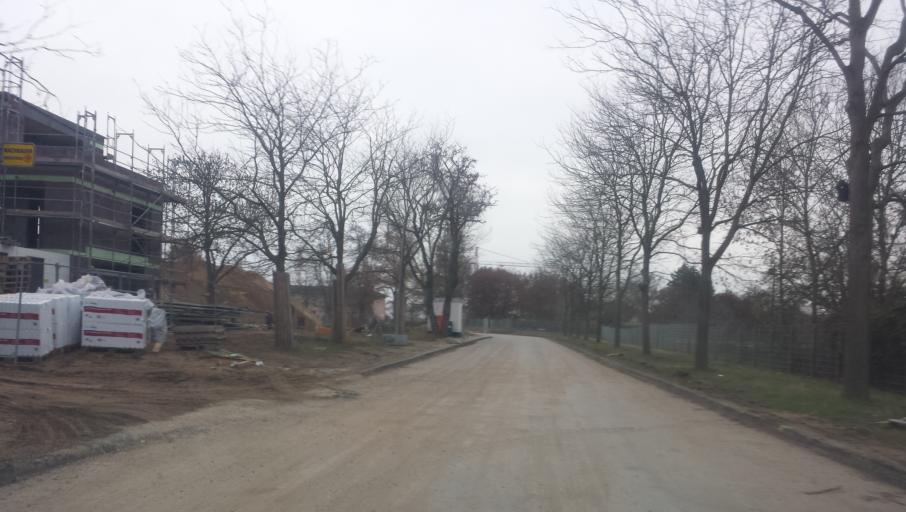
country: DE
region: Hesse
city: Viernheim
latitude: 49.5236
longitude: 8.5289
